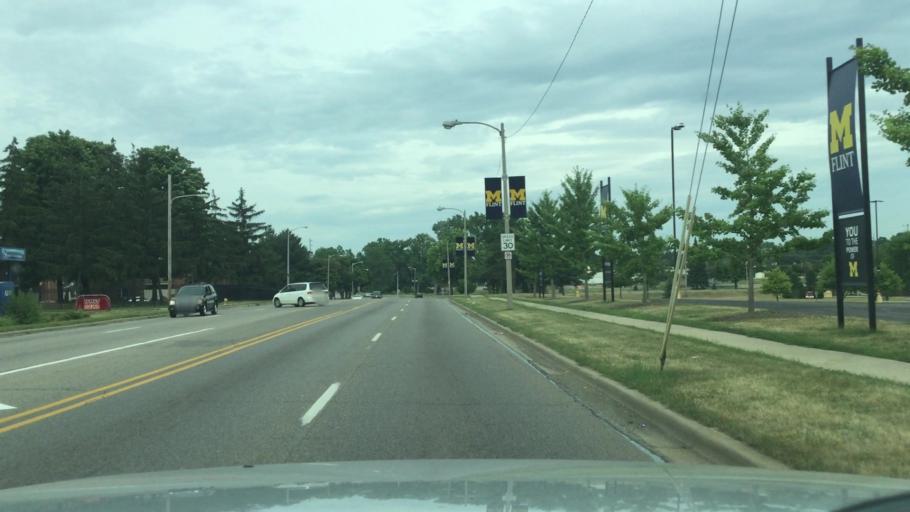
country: US
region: Michigan
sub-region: Genesee County
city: Flint
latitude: 43.0235
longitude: -83.6921
